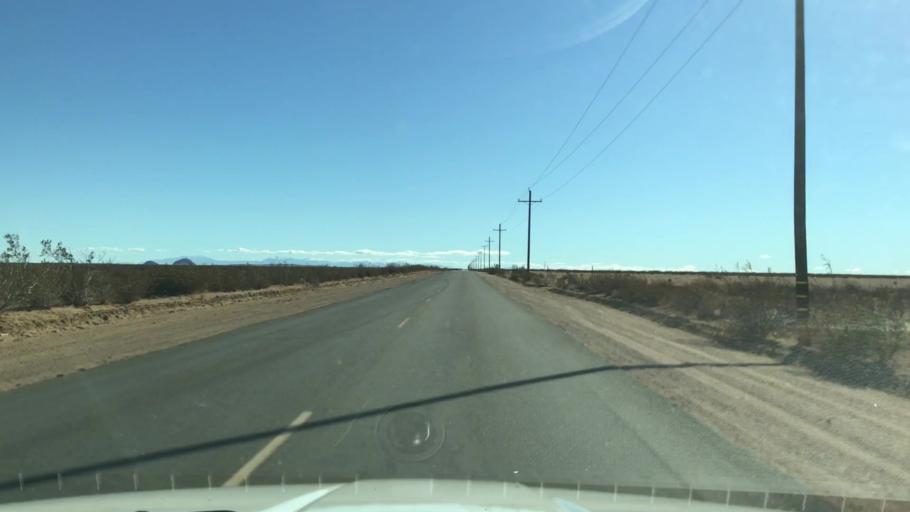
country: US
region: California
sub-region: Kern County
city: California City
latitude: 35.2067
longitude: -117.9859
